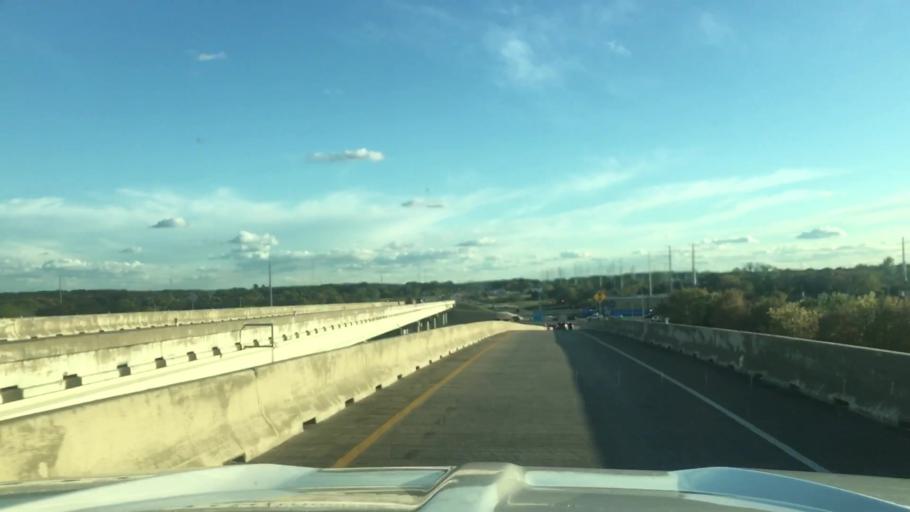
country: US
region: Texas
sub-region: Denton County
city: Denton
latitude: 33.2355
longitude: -97.0901
